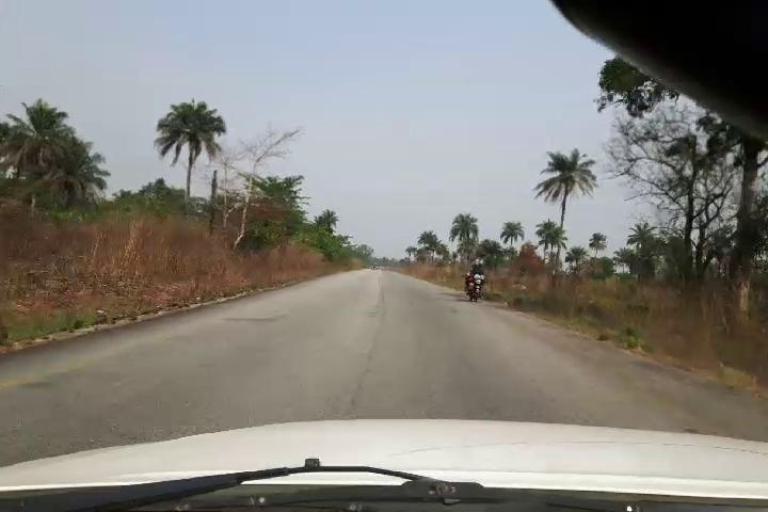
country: SL
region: Southern Province
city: Largo
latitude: 8.3085
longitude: -12.2098
